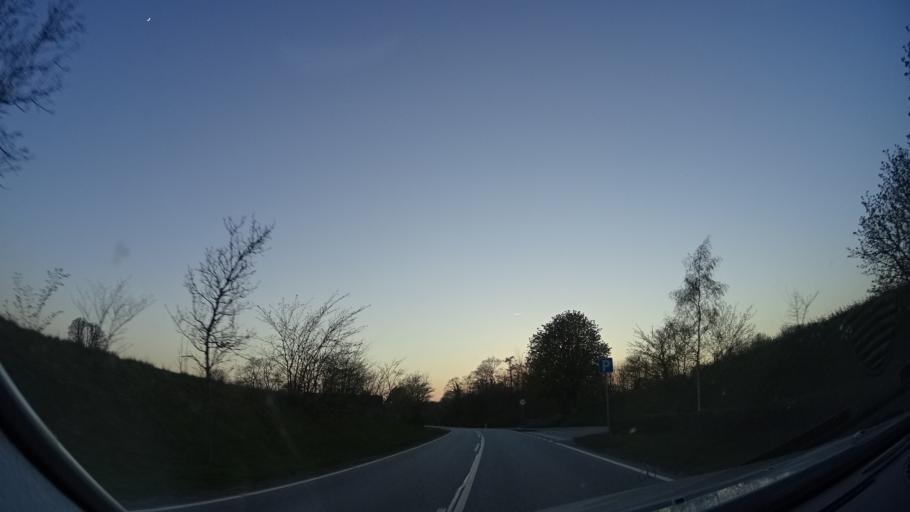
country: DK
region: Zealand
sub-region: Lejre Kommune
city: Ejby
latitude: 55.6724
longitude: 11.8690
